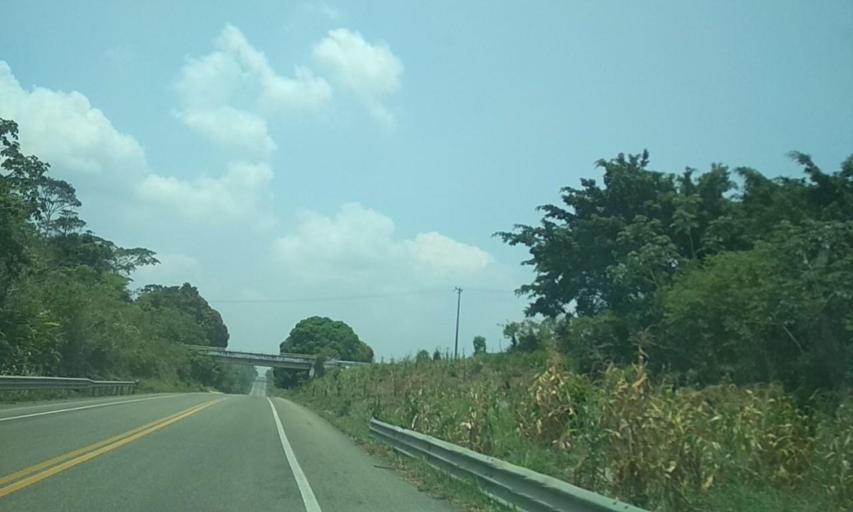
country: MX
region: Tabasco
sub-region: Huimanguillo
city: Francisco Rueda
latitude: 17.6728
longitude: -93.8734
